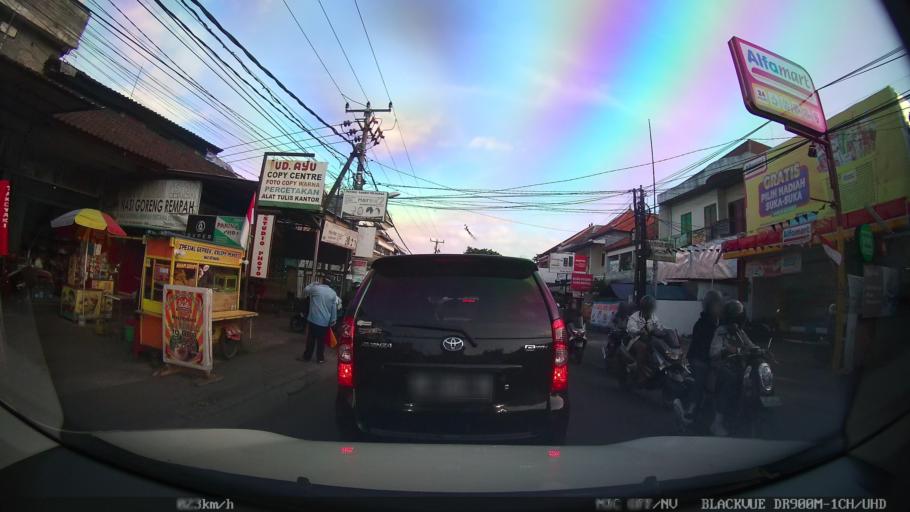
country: ID
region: Bali
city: Banjar Kertasari
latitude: -8.6312
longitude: 115.2098
